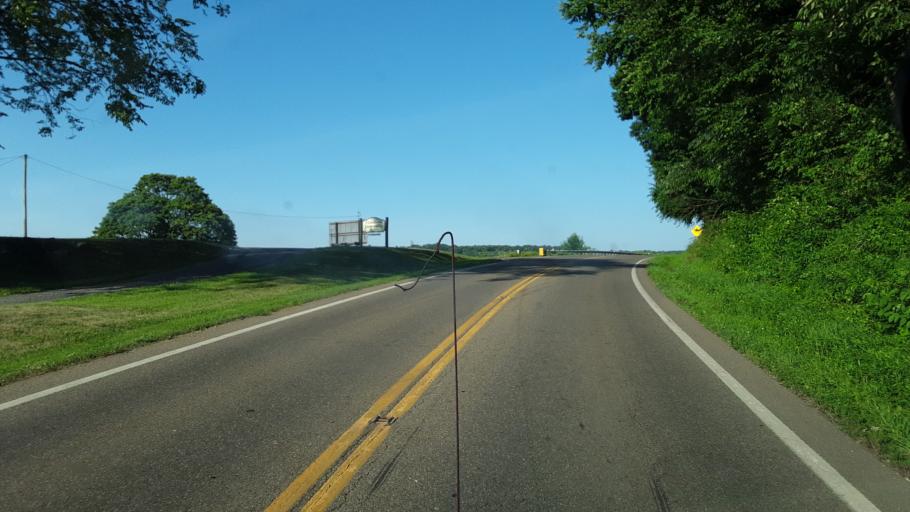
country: US
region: Ohio
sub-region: Tuscarawas County
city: New Philadelphia
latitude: 40.4971
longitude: -81.4262
